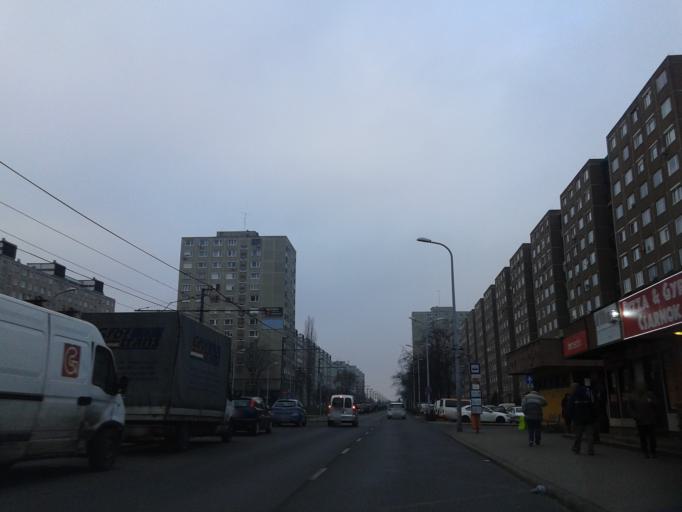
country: HU
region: Budapest
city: Budapest XV. keruelet
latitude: 47.5453
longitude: 19.1386
